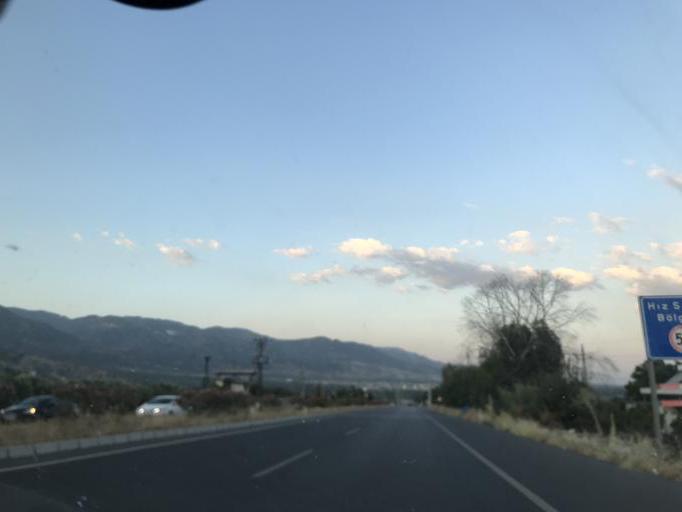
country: TR
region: Aydin
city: Buharkent
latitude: 37.9562
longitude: 28.7036
